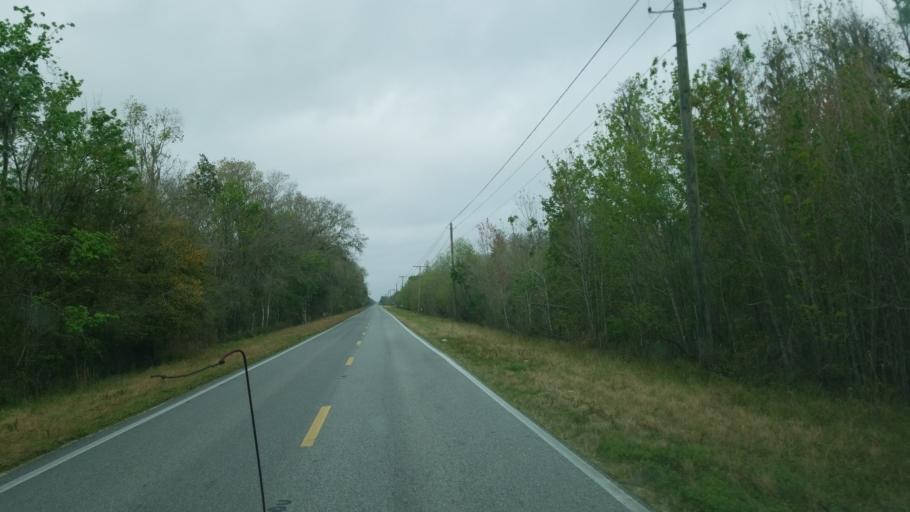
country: US
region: Florida
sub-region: Polk County
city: Polk City
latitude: 28.2590
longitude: -81.8995
